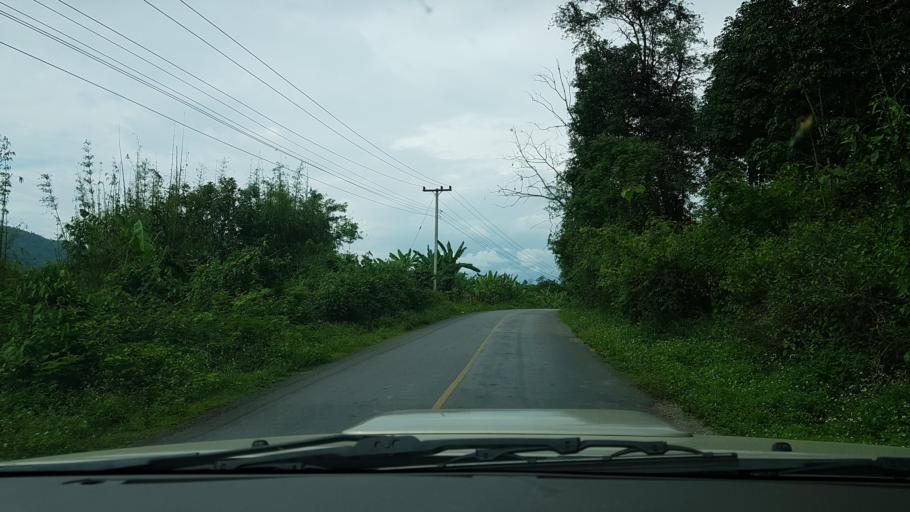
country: LA
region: Loungnamtha
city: Muang Nale
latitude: 20.3772
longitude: 101.7379
